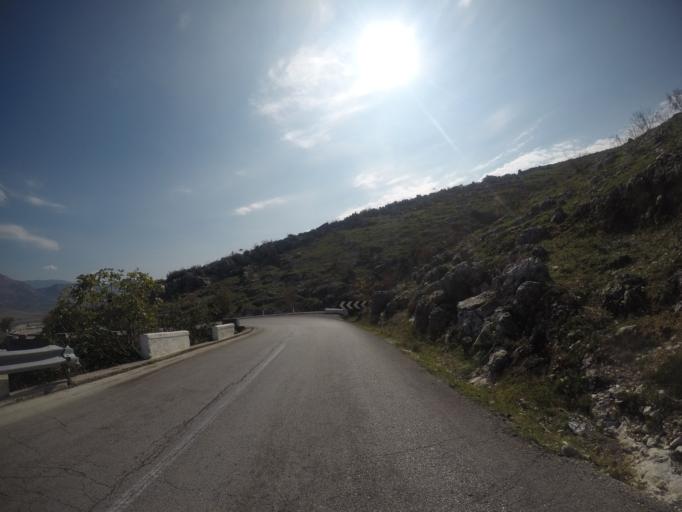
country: AL
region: Gjirokaster
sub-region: Rrethi i Gjirokastres
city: Libohove
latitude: 39.9482
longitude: 20.2481
